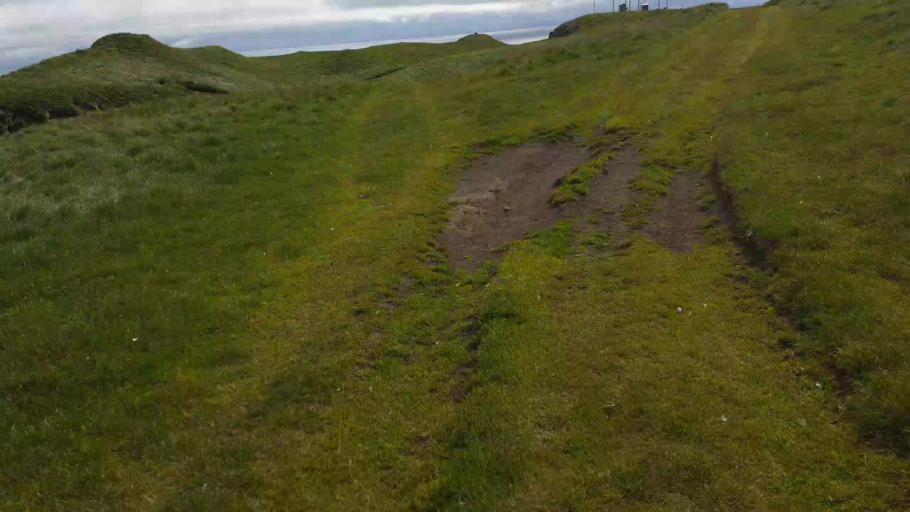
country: IS
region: Northeast
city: Dalvik
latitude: 66.5491
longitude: -17.9918
